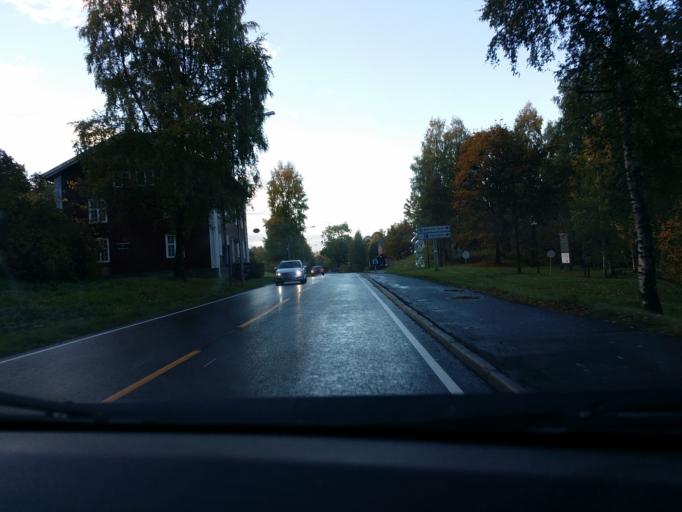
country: NO
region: Akershus
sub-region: Baerum
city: Sandvika
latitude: 59.9384
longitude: 10.5021
